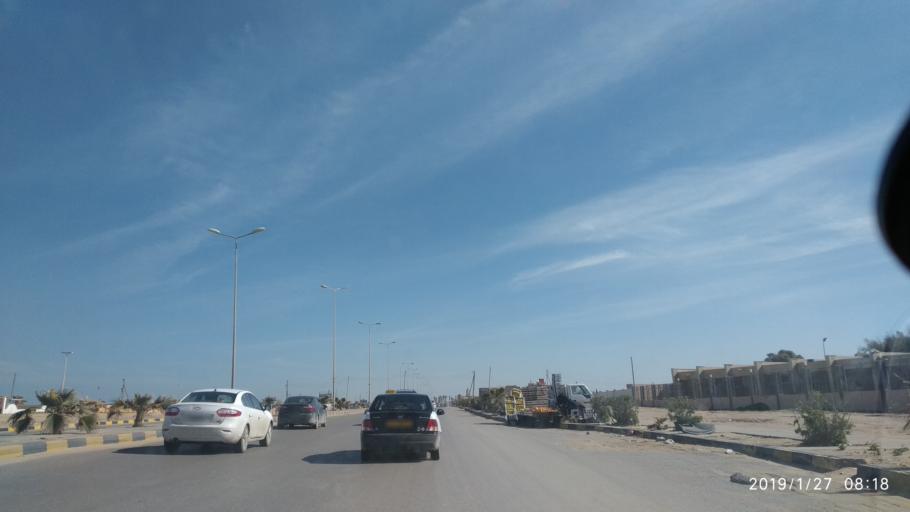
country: LY
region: Tripoli
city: Tagiura
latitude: 32.8955
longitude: 13.3256
